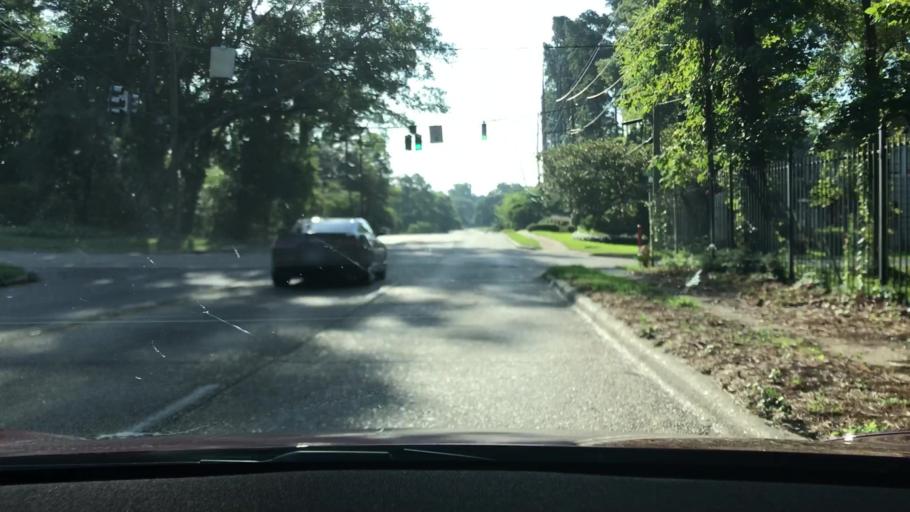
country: US
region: Louisiana
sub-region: Bossier Parish
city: Bossier City
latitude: 32.4547
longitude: -93.7377
